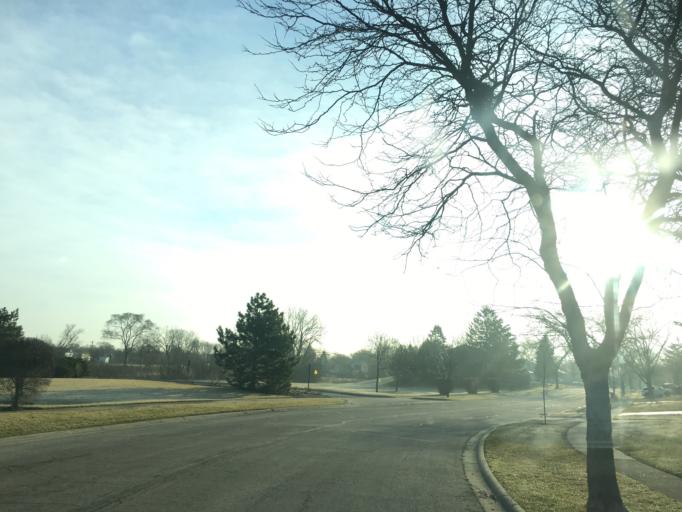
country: US
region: Illinois
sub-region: Cook County
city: Schaumburg
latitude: 42.0357
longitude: -88.1154
